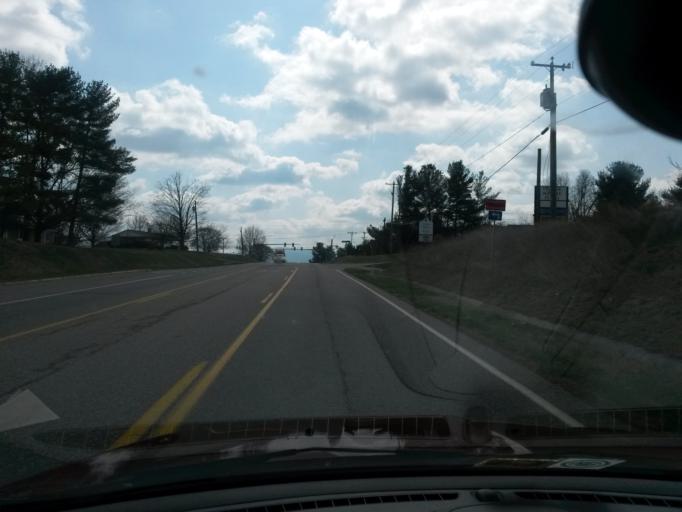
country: US
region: Virginia
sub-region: Augusta County
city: Weyers Cave
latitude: 38.2859
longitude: -78.9146
